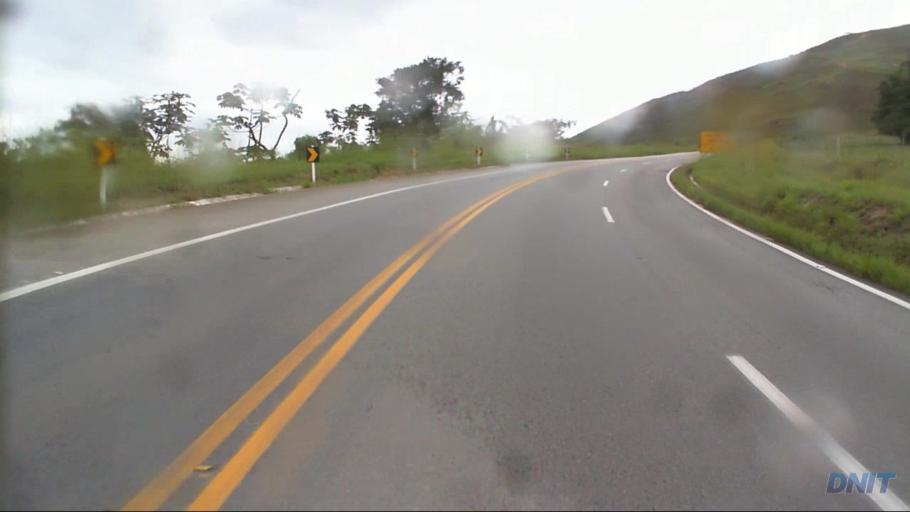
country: BR
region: Minas Gerais
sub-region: Nova Era
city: Nova Era
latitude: -19.6786
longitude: -42.9796
